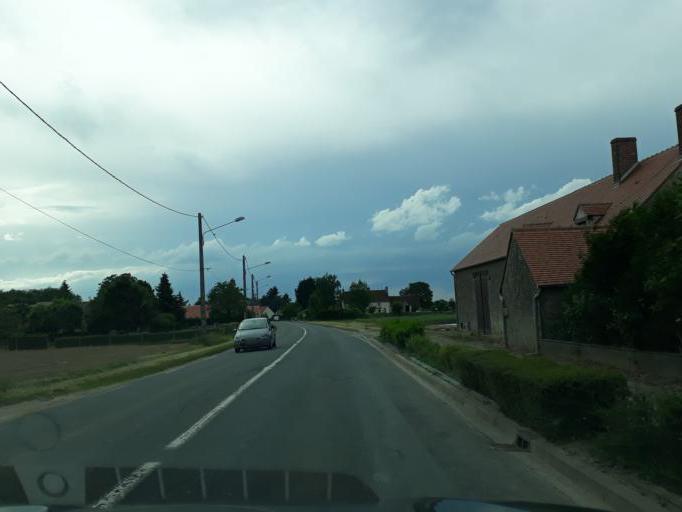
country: FR
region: Centre
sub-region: Departement du Loiret
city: Darvoy
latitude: 47.8539
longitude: 2.0898
